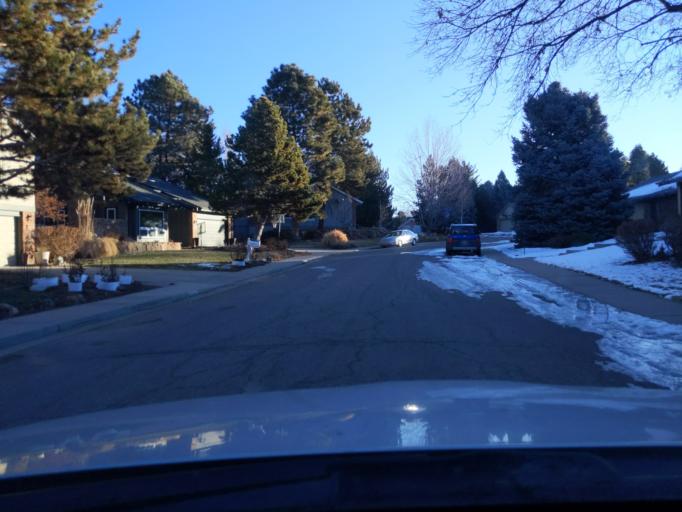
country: US
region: Colorado
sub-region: Arapahoe County
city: Centennial
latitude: 39.5768
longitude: -104.8883
